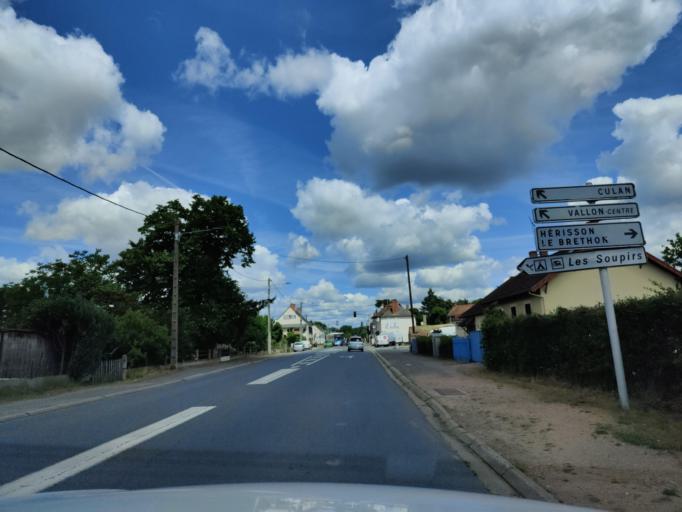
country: FR
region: Auvergne
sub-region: Departement de l'Allier
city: Vallon-en-Sully
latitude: 46.5318
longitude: 2.6212
